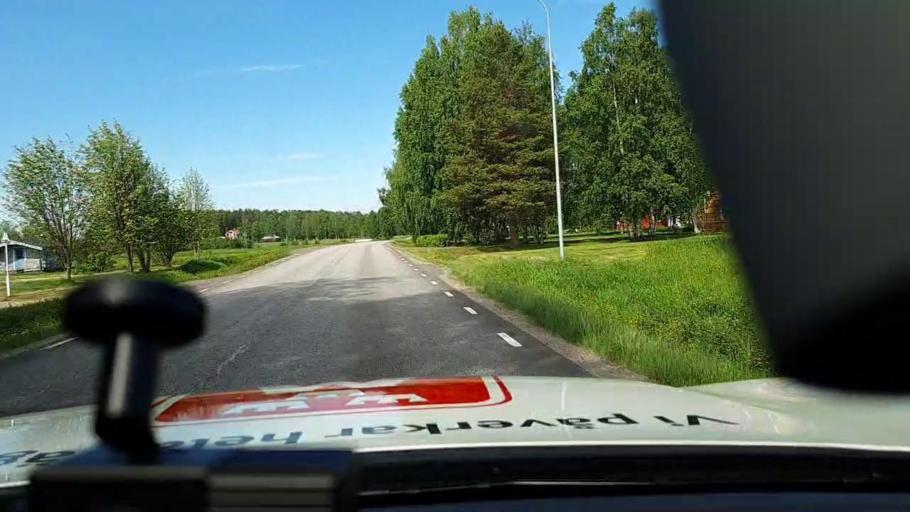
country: SE
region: Norrbotten
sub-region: Lulea Kommun
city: Sodra Sunderbyn
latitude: 65.6547
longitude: 21.8536
